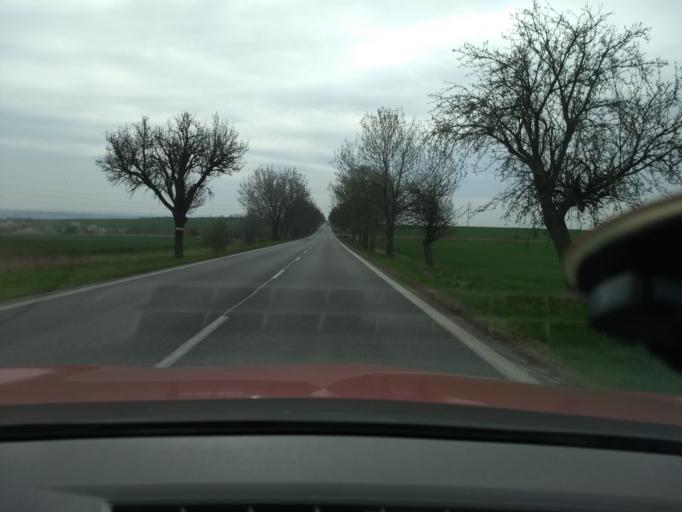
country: CZ
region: Central Bohemia
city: Horomerice
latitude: 50.1245
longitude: 14.3504
